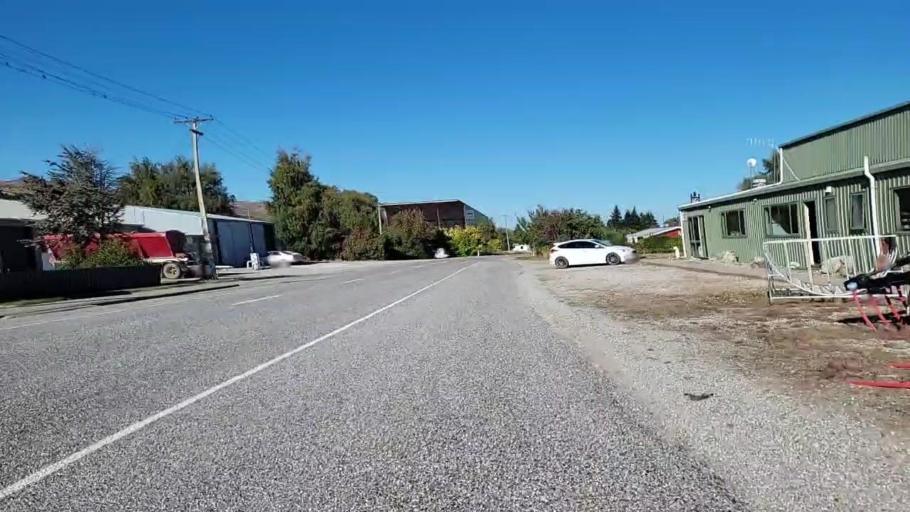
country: NZ
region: Otago
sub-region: Queenstown-Lakes District
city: Wanaka
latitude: -45.0072
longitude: 169.9126
